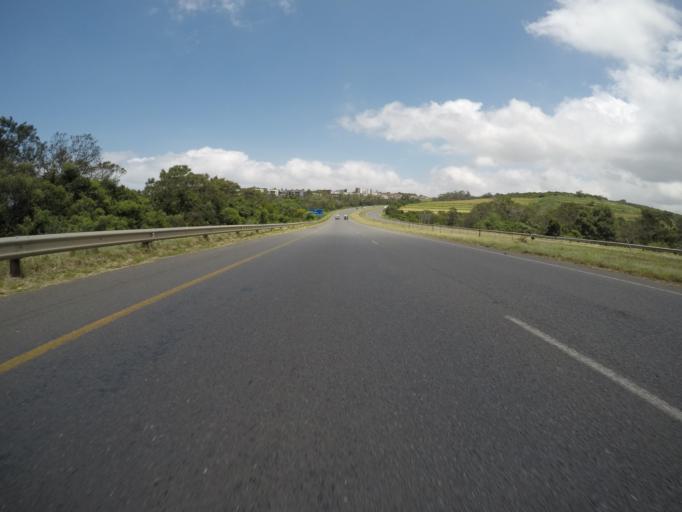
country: ZA
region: Eastern Cape
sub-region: Buffalo City Metropolitan Municipality
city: East London
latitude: -32.9439
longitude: 27.9424
